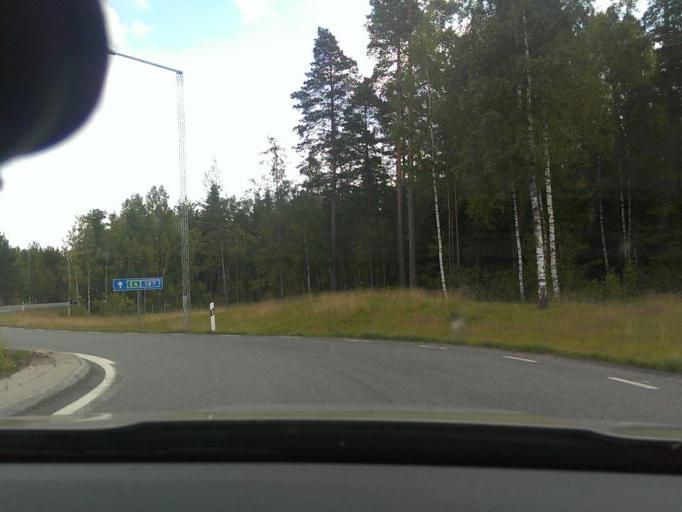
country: SE
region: Joenkoeping
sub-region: Varnamo Kommun
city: Varnamo
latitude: 57.1930
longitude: 14.0643
